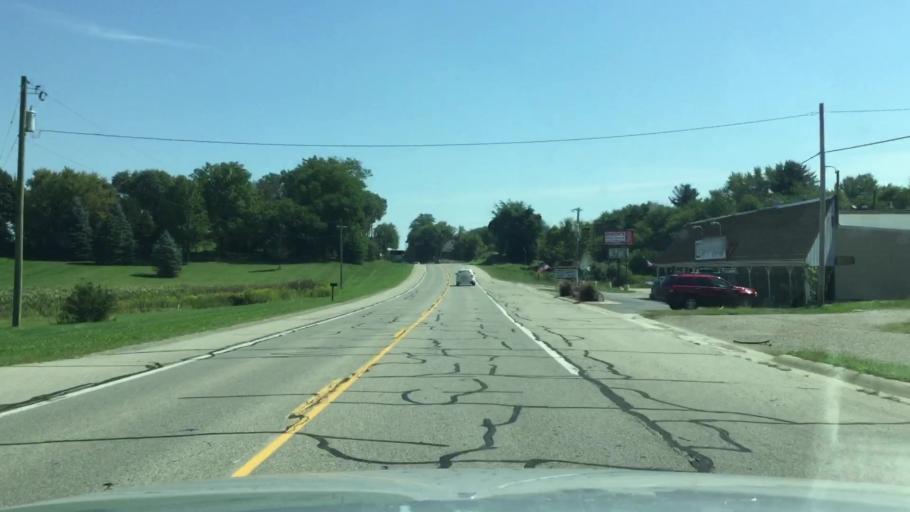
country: US
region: Michigan
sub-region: Lenawee County
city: Clinton
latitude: 42.0711
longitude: -84.0079
